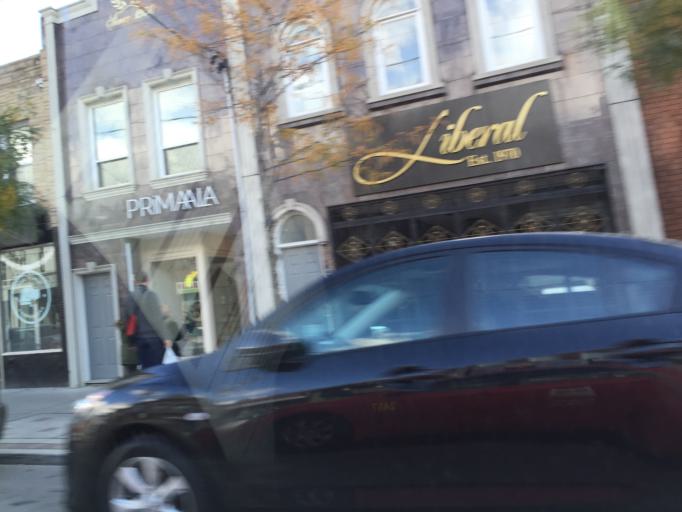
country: CA
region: Ontario
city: Toronto
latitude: 43.6518
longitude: -79.4083
